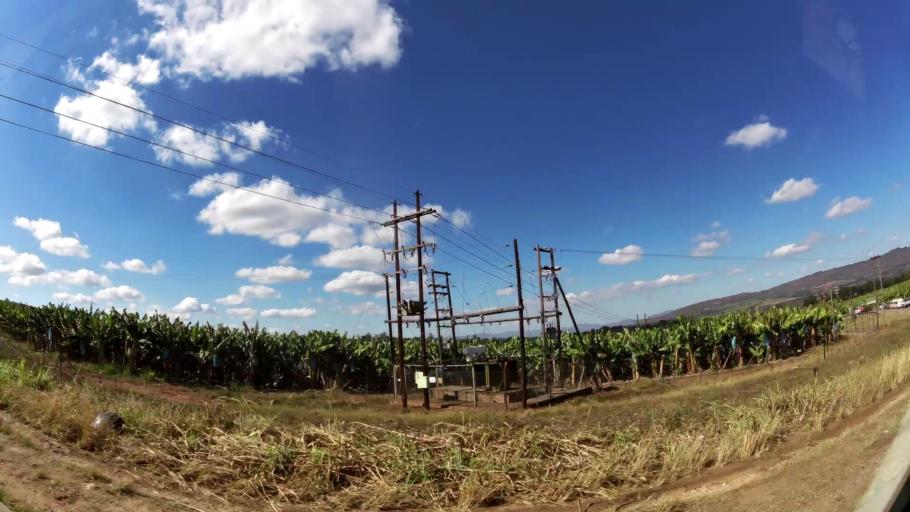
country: ZA
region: Limpopo
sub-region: Mopani District Municipality
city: Tzaneen
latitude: -23.8129
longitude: 30.1730
